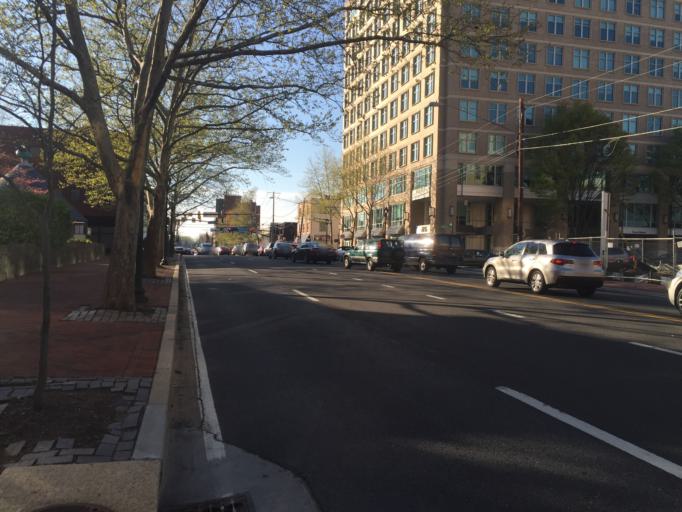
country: US
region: Maryland
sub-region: Montgomery County
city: Bethesda
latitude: 38.9866
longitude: -77.0976
